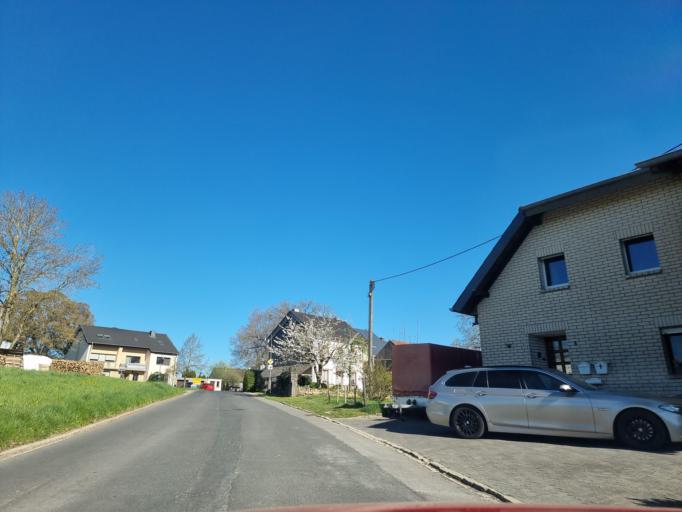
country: DE
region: Rheinland-Pfalz
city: Idenheim
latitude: 49.8972
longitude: 6.5706
